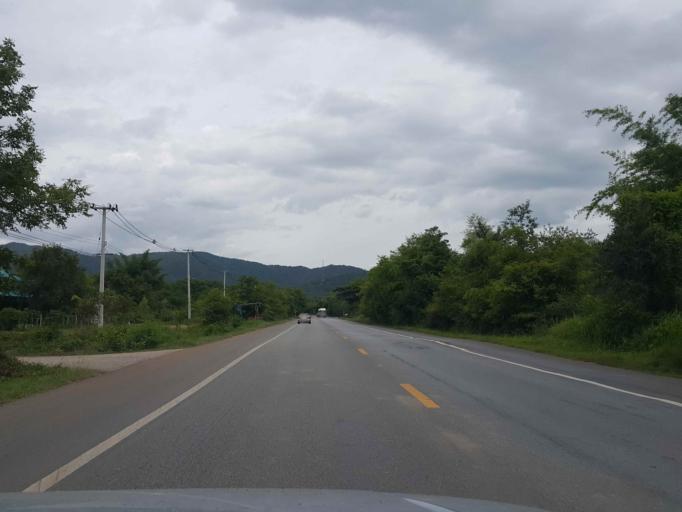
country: TH
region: Lampang
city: Lampang
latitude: 18.2511
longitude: 99.5303
